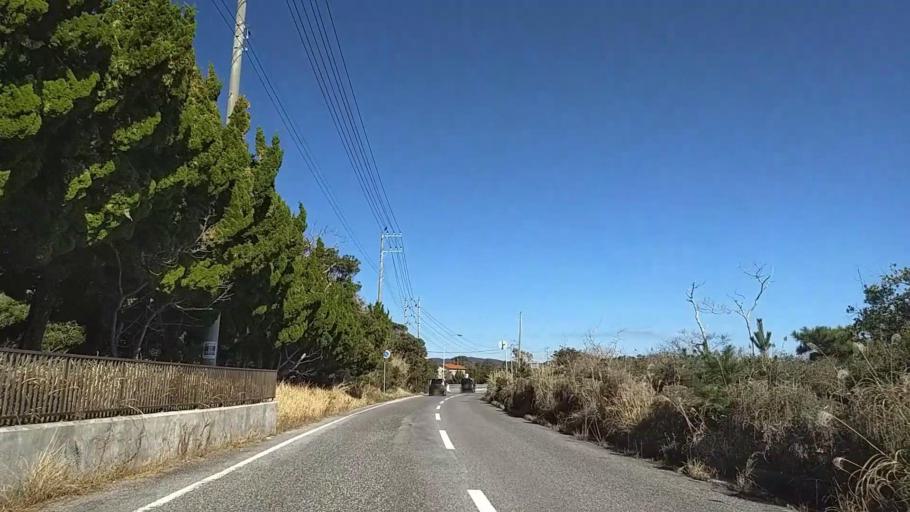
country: JP
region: Chiba
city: Tateyama
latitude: 35.0095
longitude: 139.9773
